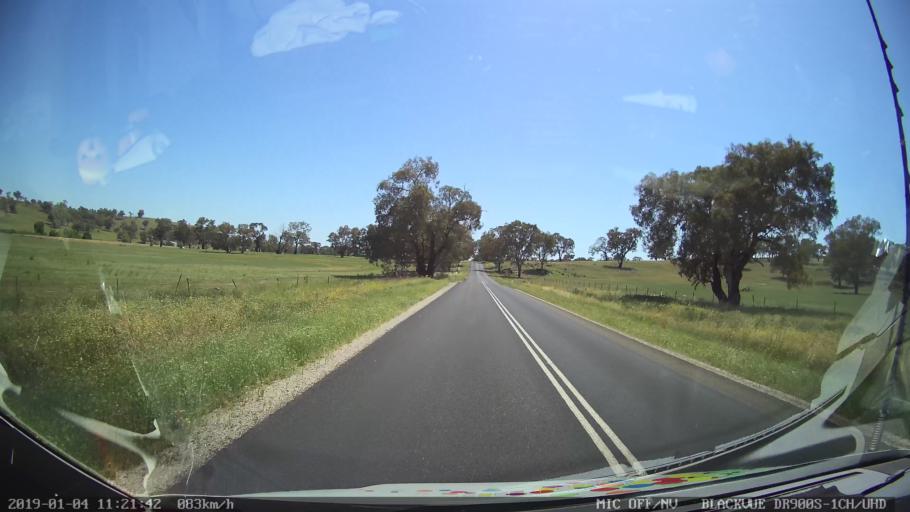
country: AU
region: New South Wales
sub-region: Cabonne
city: Molong
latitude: -33.1526
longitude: 148.7142
